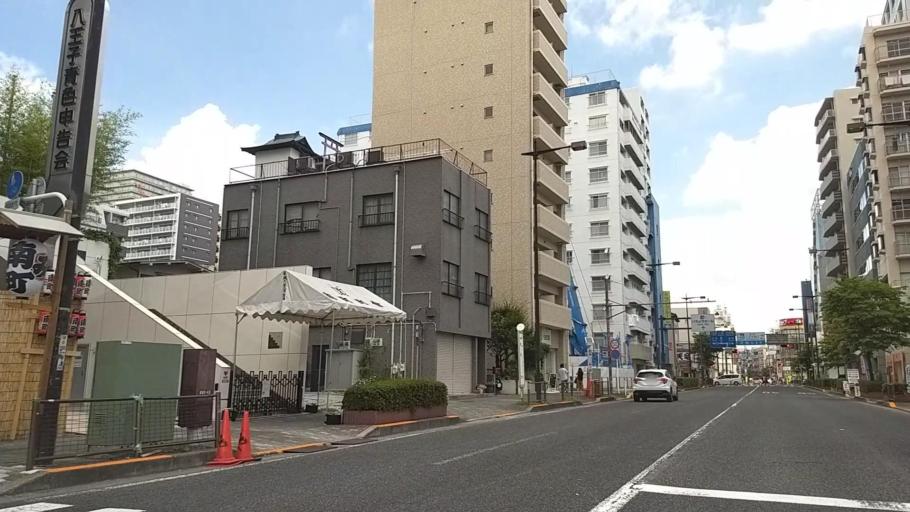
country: JP
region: Tokyo
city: Hachioji
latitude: 35.6580
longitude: 139.3332
